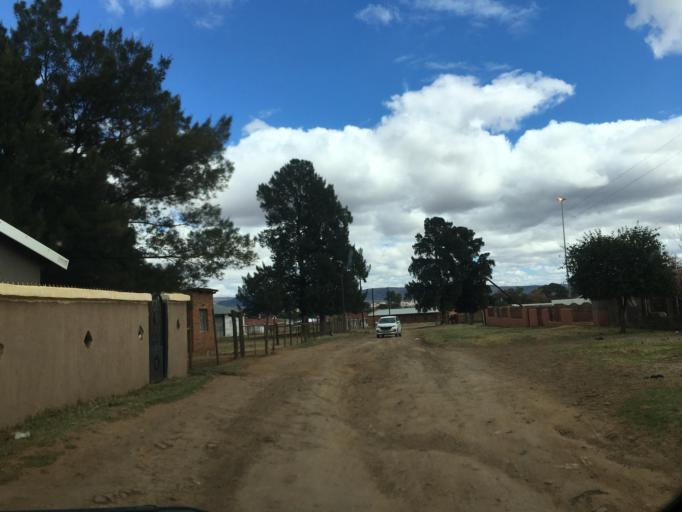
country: ZA
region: Eastern Cape
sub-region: Chris Hani District Municipality
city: Cala
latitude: -31.5317
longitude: 27.6956
